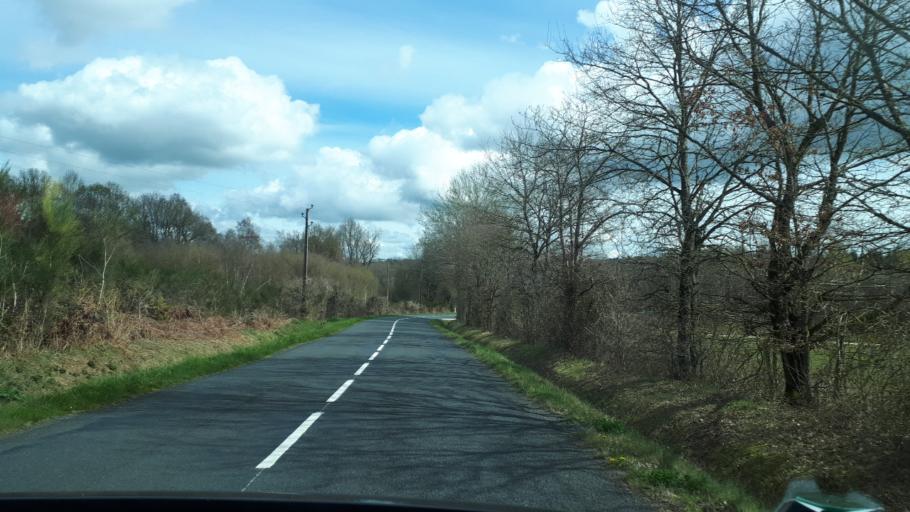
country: FR
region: Pays de la Loire
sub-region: Departement de la Sarthe
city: Brette-les-Pins
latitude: 47.8708
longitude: 0.3858
